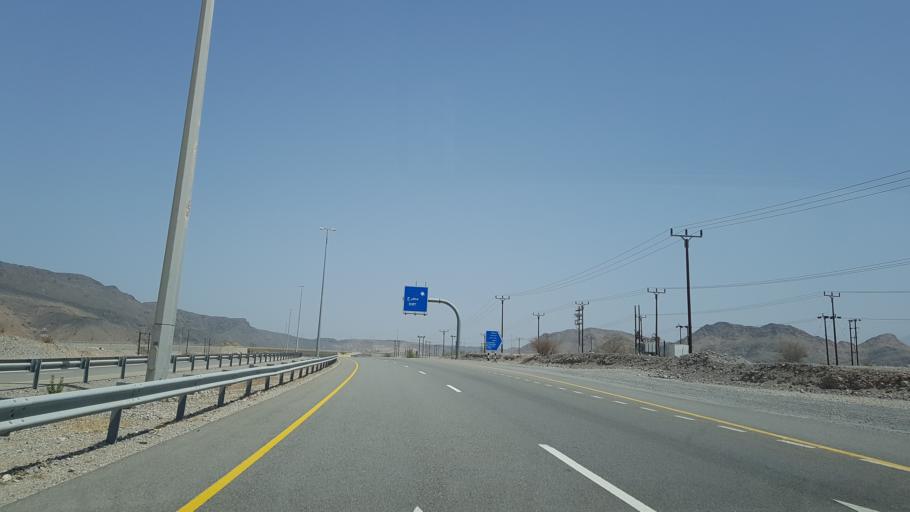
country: OM
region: Muhafazat Masqat
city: Muscat
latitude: 23.2491
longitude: 58.7853
